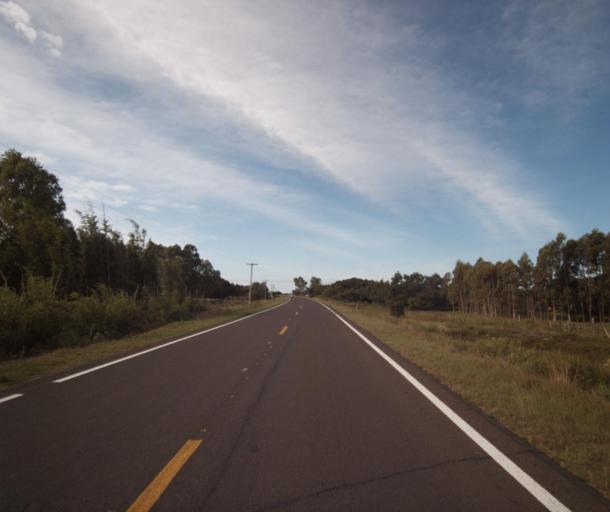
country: BR
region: Rio Grande do Sul
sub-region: Tapes
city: Tapes
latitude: -31.3272
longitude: -51.1261
